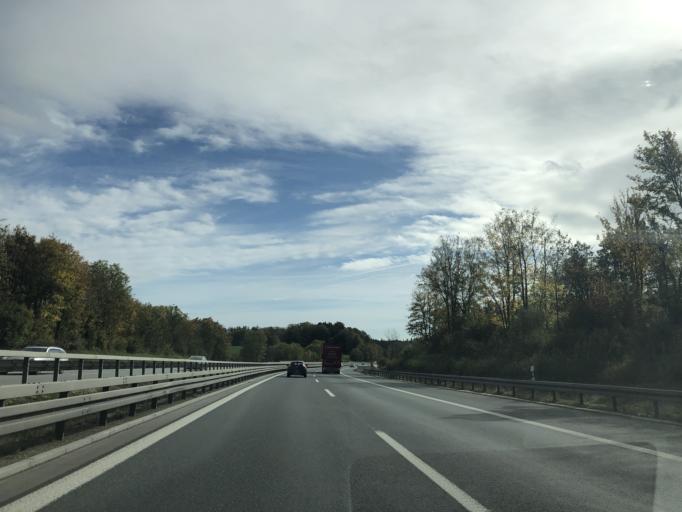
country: DE
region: Bavaria
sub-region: Upper Palatinate
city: Pilsach
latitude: 49.2944
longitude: 11.5559
